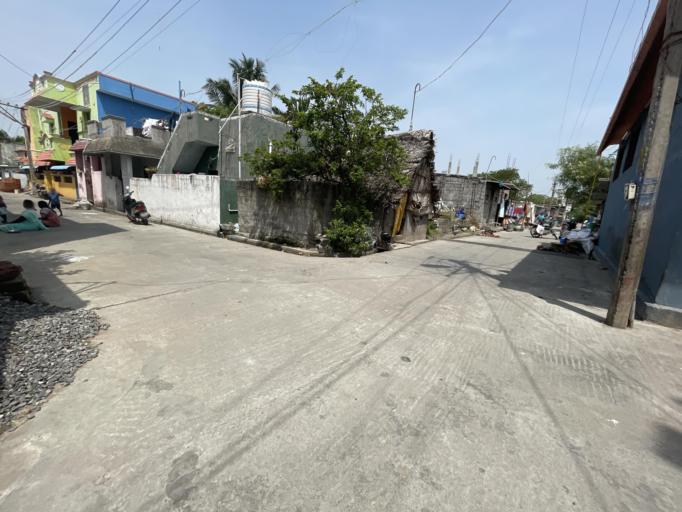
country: IN
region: Tamil Nadu
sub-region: Villupuram
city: Auroville
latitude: 11.9774
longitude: 79.7220
